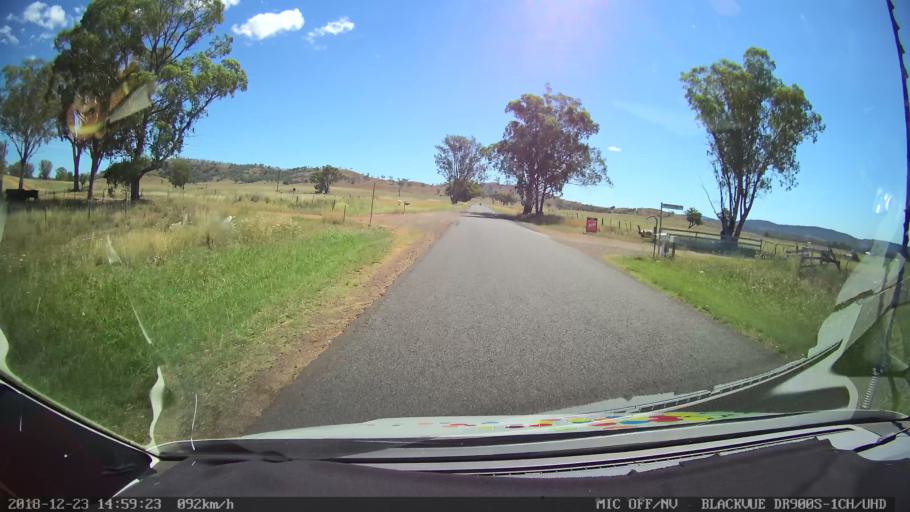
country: AU
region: New South Wales
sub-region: Tamworth Municipality
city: Manilla
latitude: -30.7235
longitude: 150.8013
